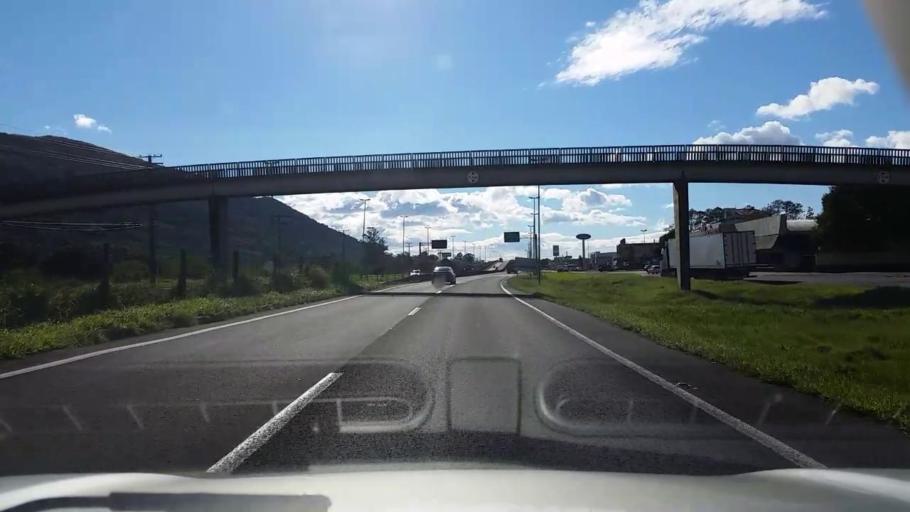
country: BR
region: Rio Grande do Sul
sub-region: Osorio
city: Osorio
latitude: -29.8881
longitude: -50.2768
